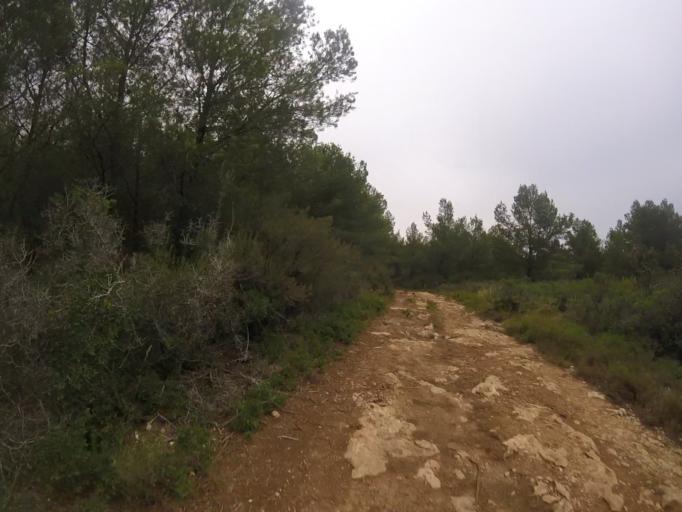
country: ES
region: Valencia
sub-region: Provincia de Castello
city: Alcoceber
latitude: 40.2857
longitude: 0.2853
